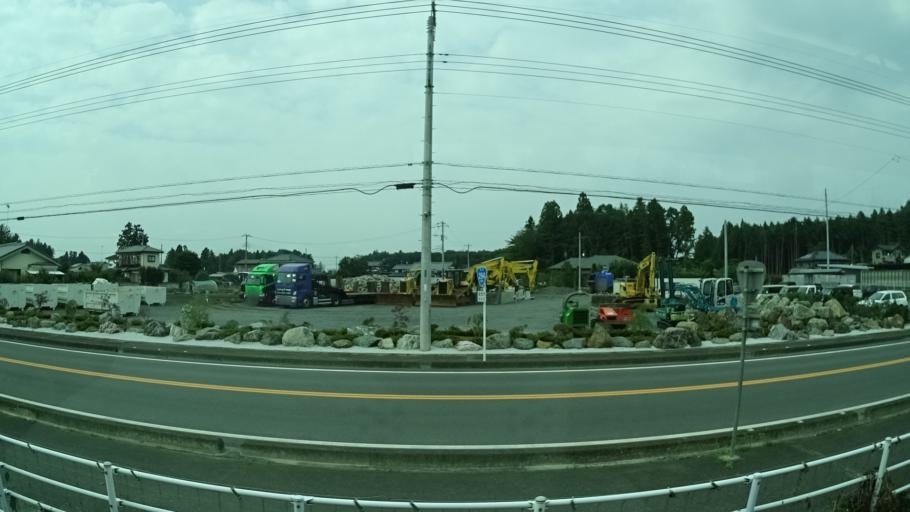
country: JP
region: Tochigi
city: Mashiko
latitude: 36.4555
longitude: 140.0657
